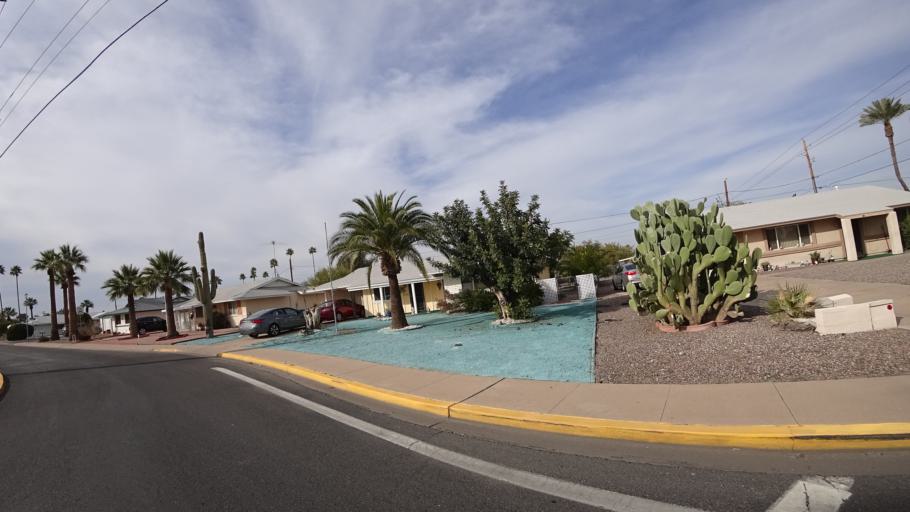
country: US
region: Arizona
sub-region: Maricopa County
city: Youngtown
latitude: 33.5948
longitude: -112.2903
